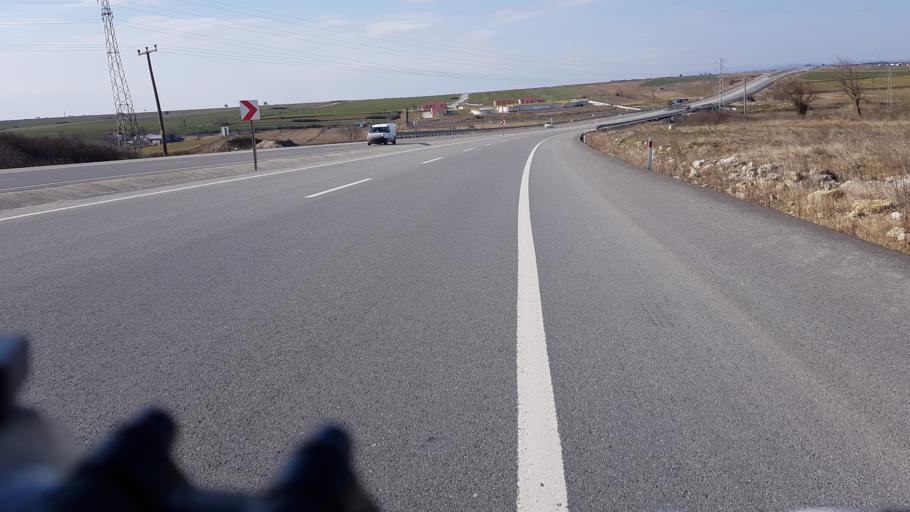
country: TR
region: Tekirdag
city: Saray
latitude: 41.4224
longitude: 27.9152
